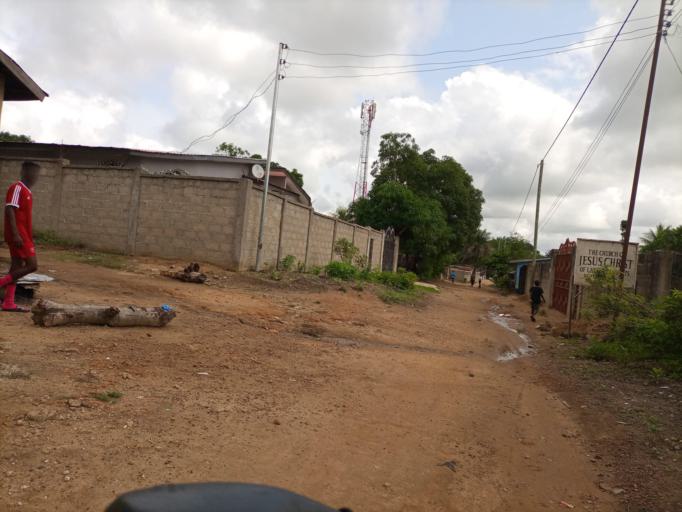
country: SL
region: Southern Province
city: Bo
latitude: 7.9652
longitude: -11.7600
